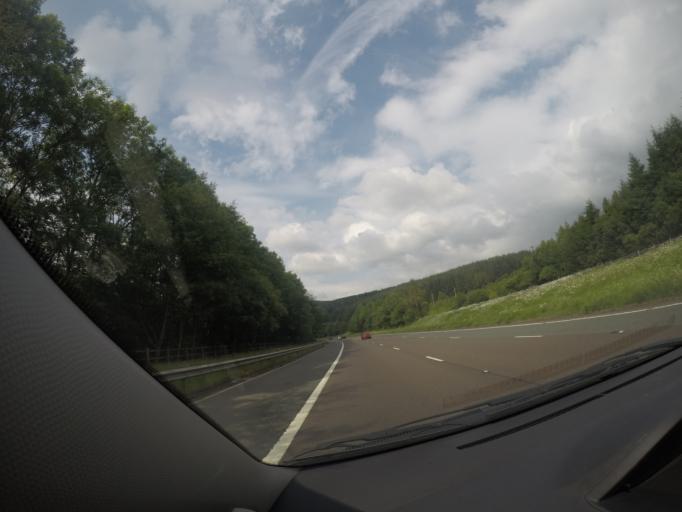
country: GB
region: Scotland
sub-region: Dumfries and Galloway
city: Moffat
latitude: 55.3686
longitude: -3.5137
